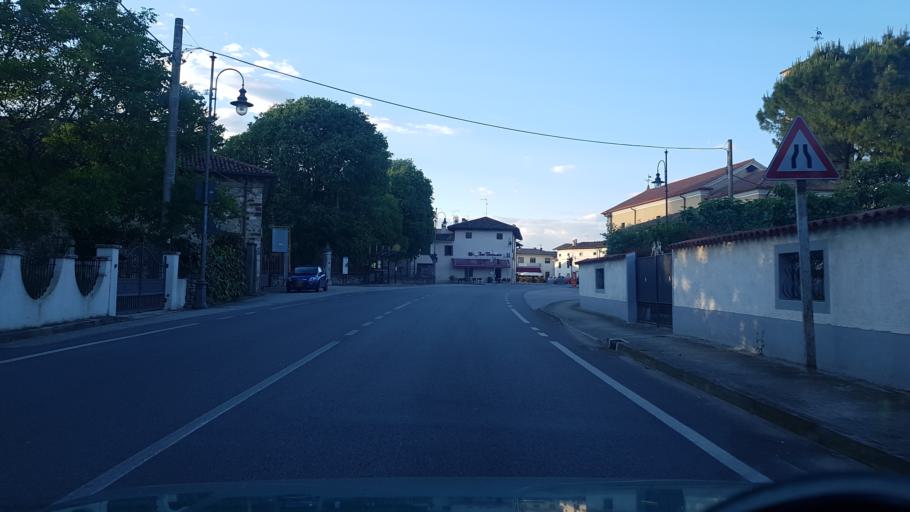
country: IT
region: Friuli Venezia Giulia
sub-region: Provincia di Udine
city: Santa Maria la Longa
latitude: 45.9217
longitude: 13.2948
